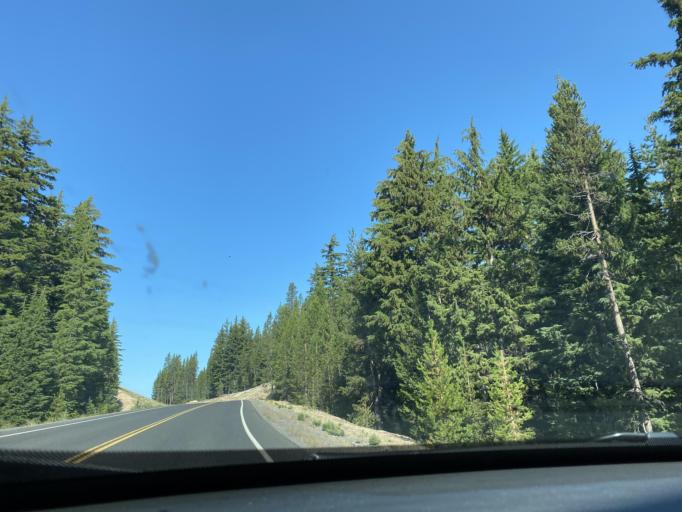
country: US
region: Oregon
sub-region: Deschutes County
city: Three Rivers
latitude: 43.7041
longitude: -121.2587
